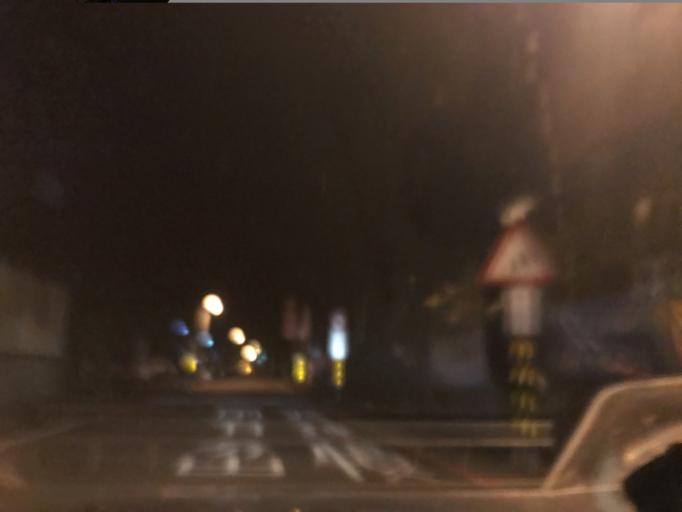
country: TW
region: Taiwan
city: Daxi
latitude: 24.8517
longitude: 121.2155
